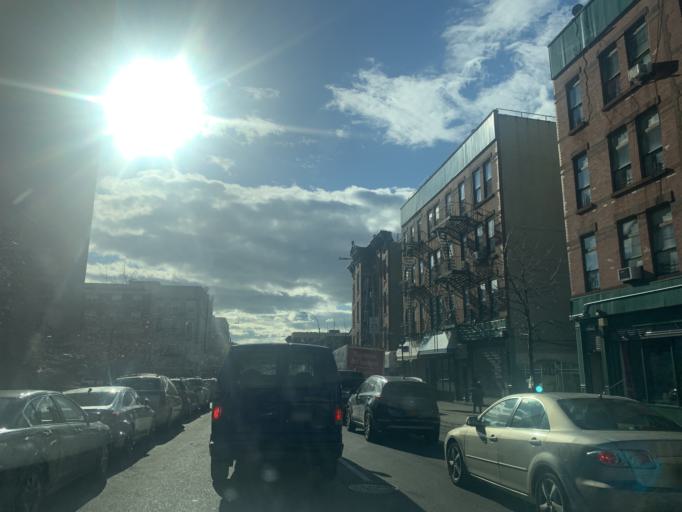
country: US
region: New York
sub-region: Kings County
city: Brooklyn
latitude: 40.6934
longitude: -73.9401
